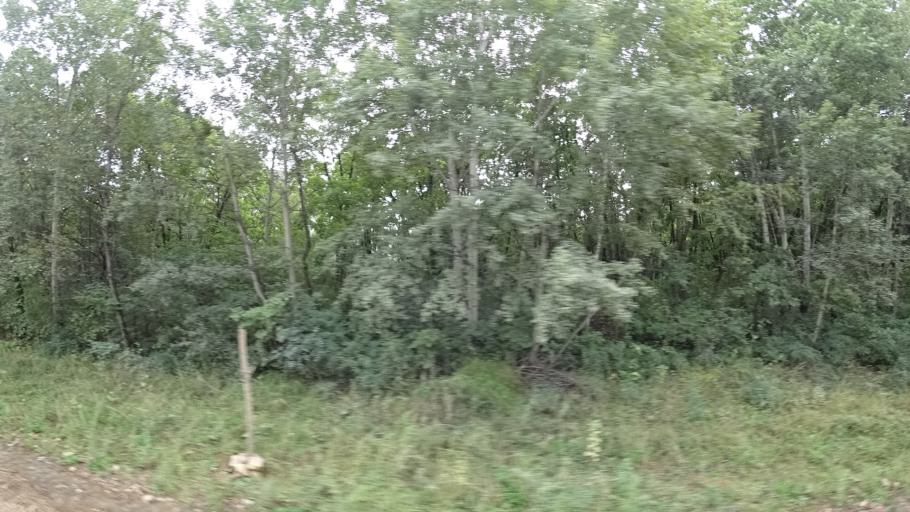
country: RU
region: Primorskiy
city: Lyalichi
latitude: 44.0834
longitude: 132.4456
